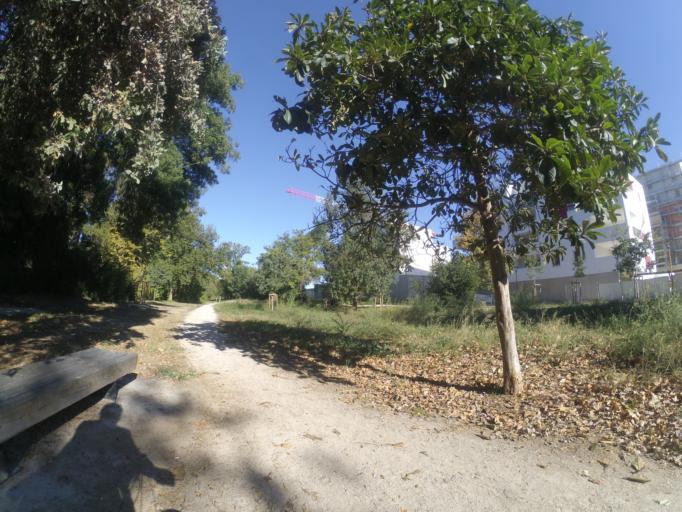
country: FR
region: Languedoc-Roussillon
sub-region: Departement des Pyrenees-Orientales
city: Perpignan
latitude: 42.6913
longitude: 2.8739
